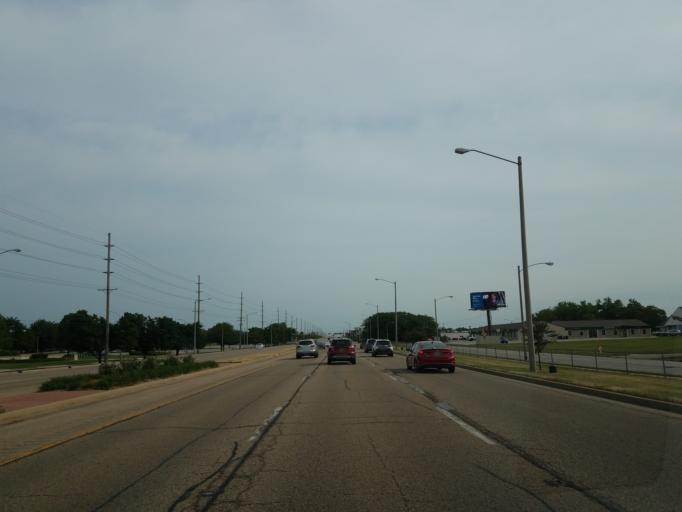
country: US
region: Illinois
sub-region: McLean County
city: Bloomington
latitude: 40.4768
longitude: -88.9525
